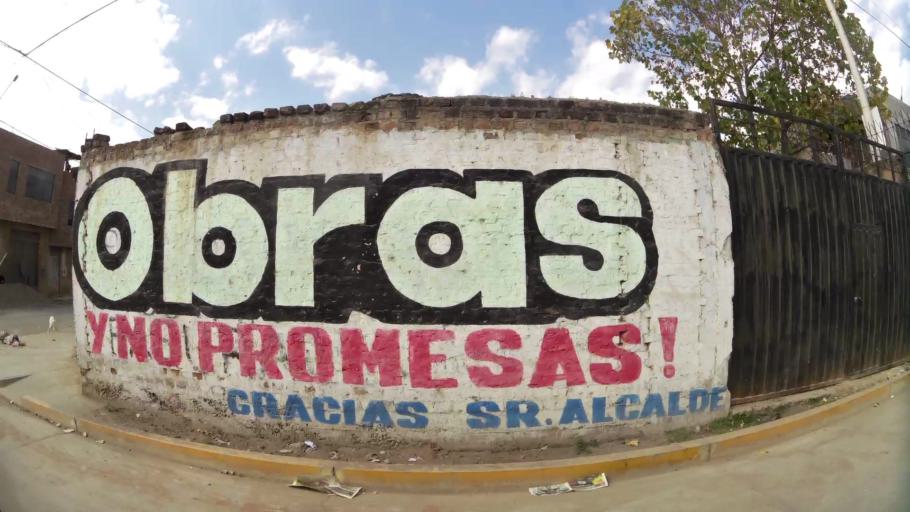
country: PE
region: Junin
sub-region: Provincia de Huancayo
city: Huancayo
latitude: -12.0930
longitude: -75.2031
